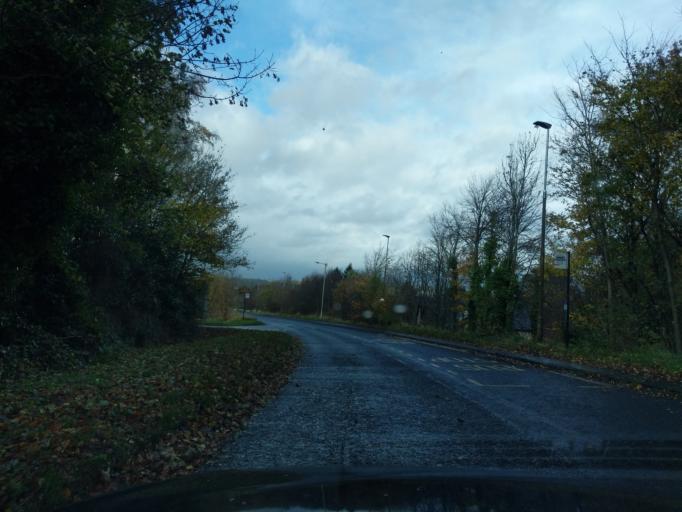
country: GB
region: Scotland
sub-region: Edinburgh
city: Newbridge
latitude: 55.9334
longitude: -3.3898
